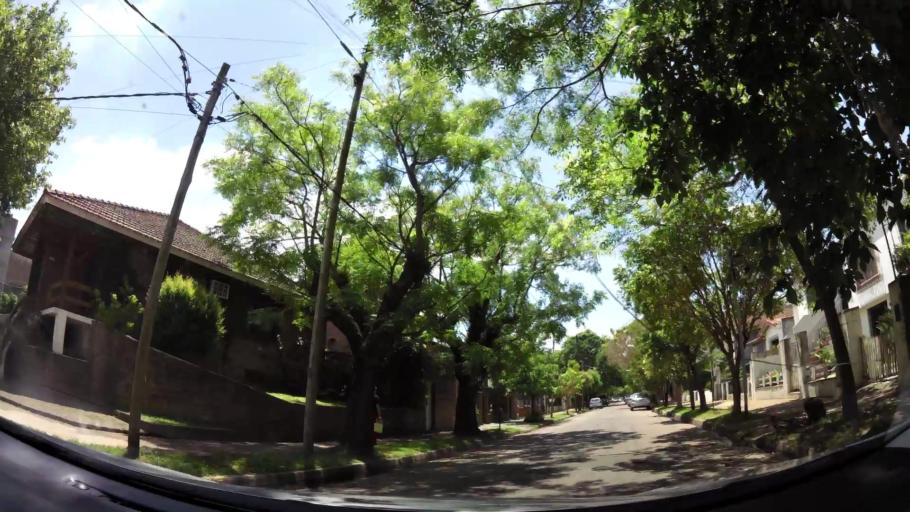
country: AR
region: Buenos Aires
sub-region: Partido de Tigre
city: Tigre
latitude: -34.4178
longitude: -58.5869
